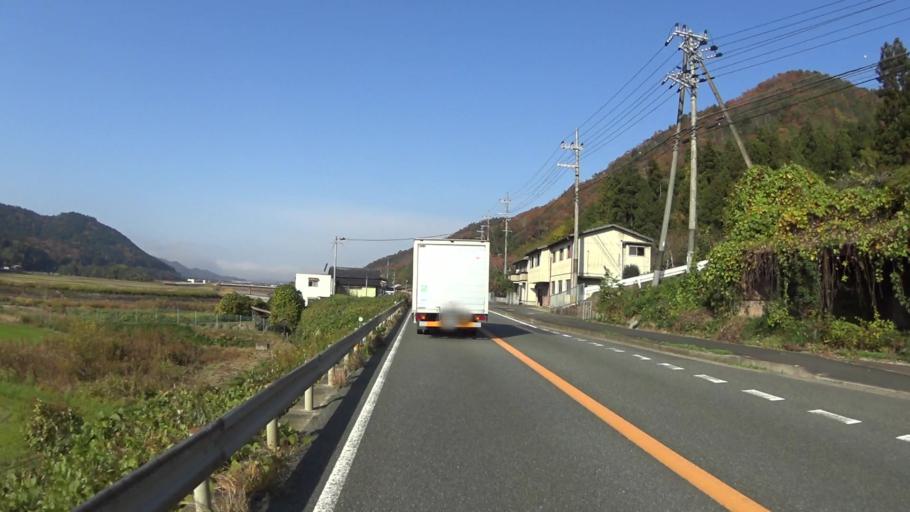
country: JP
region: Kyoto
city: Ayabe
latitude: 35.2559
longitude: 135.2023
